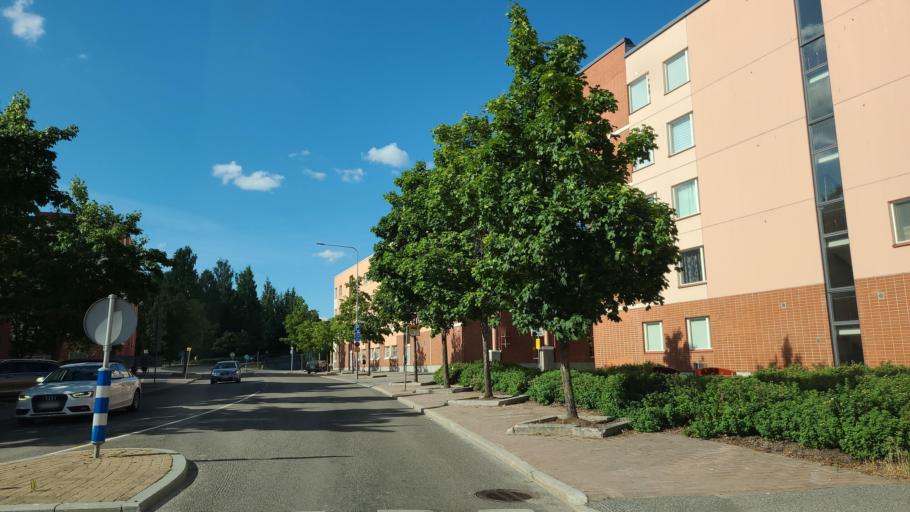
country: FI
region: Central Finland
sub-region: Jyvaeskylae
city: Jyvaeskylae
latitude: 62.2420
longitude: 25.7620
